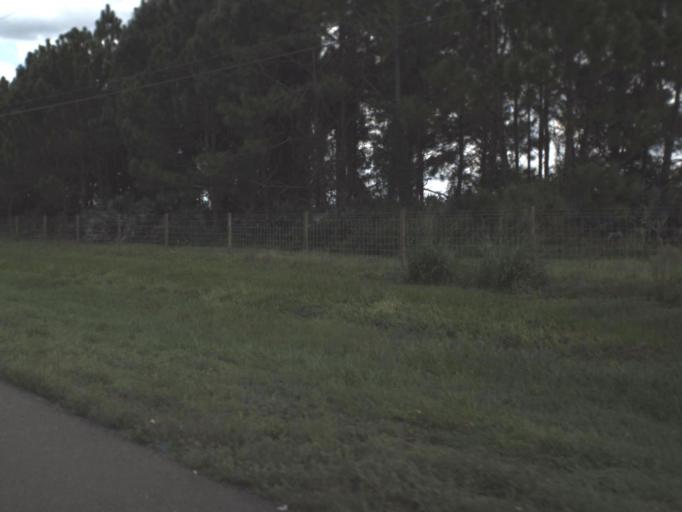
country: US
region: Florida
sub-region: Polk County
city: Highland City
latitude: 27.9967
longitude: -81.8786
